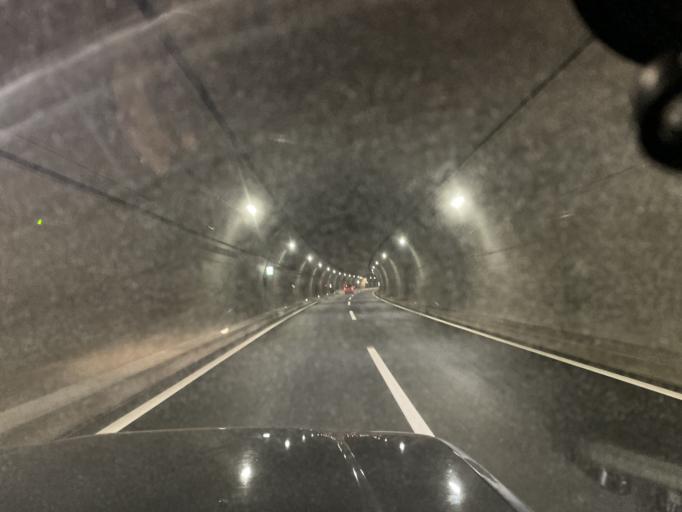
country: JP
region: Gifu
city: Gujo
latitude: 36.0189
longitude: 136.9795
